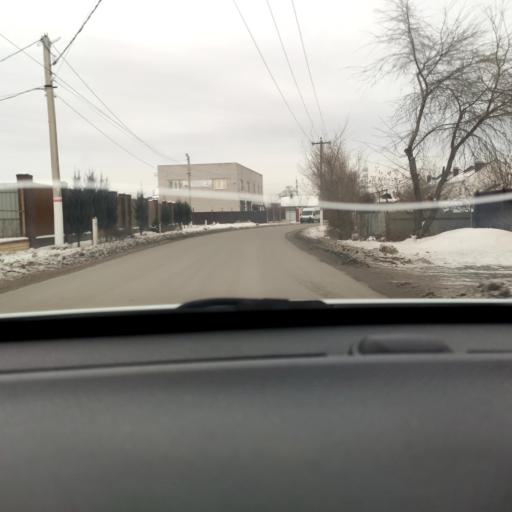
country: RU
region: Voronezj
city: Somovo
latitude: 51.6740
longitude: 39.3357
